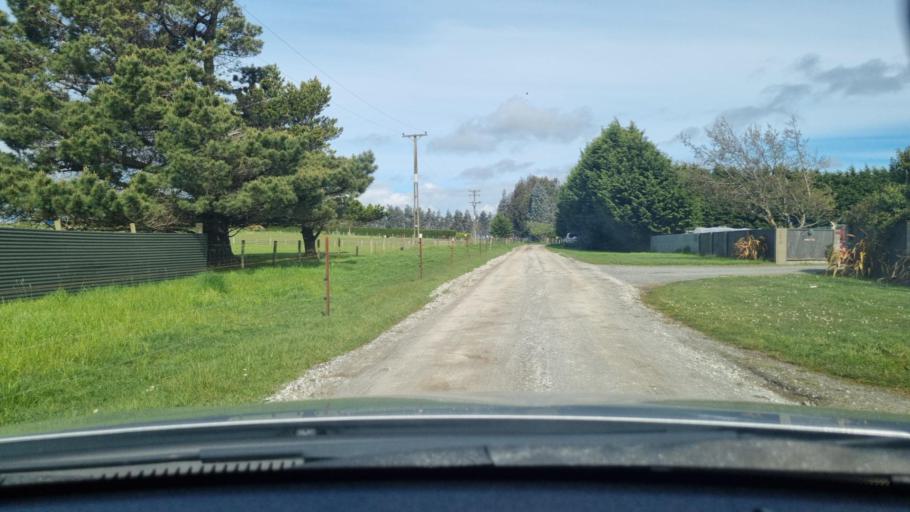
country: NZ
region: Southland
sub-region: Invercargill City
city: Invercargill
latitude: -46.4535
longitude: 168.3786
